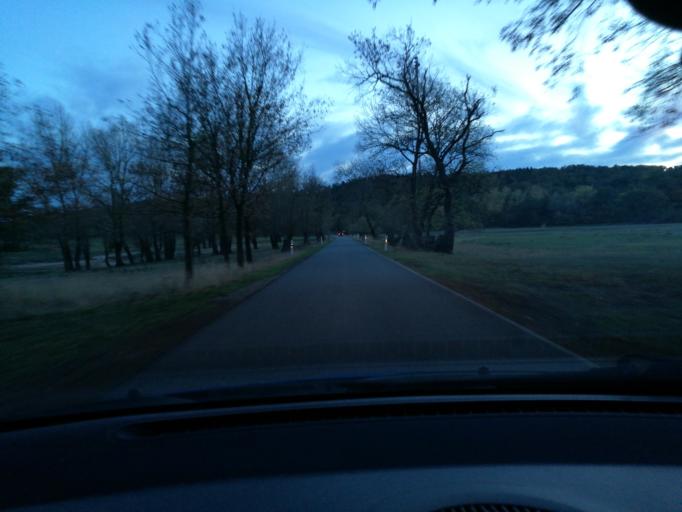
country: DE
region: Brandenburg
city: Lenzen
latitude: 53.0756
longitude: 11.4510
